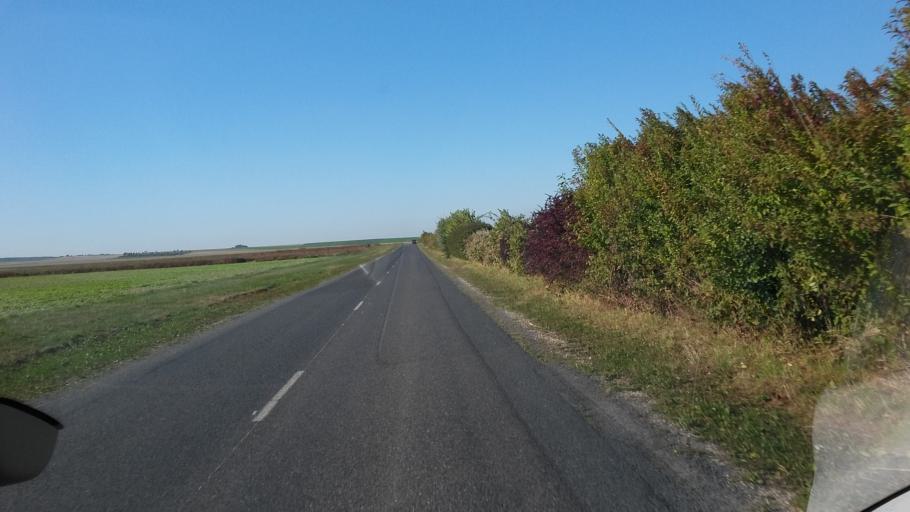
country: FR
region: Champagne-Ardenne
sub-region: Departement de la Marne
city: Connantre
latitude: 48.7430
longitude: 3.8935
